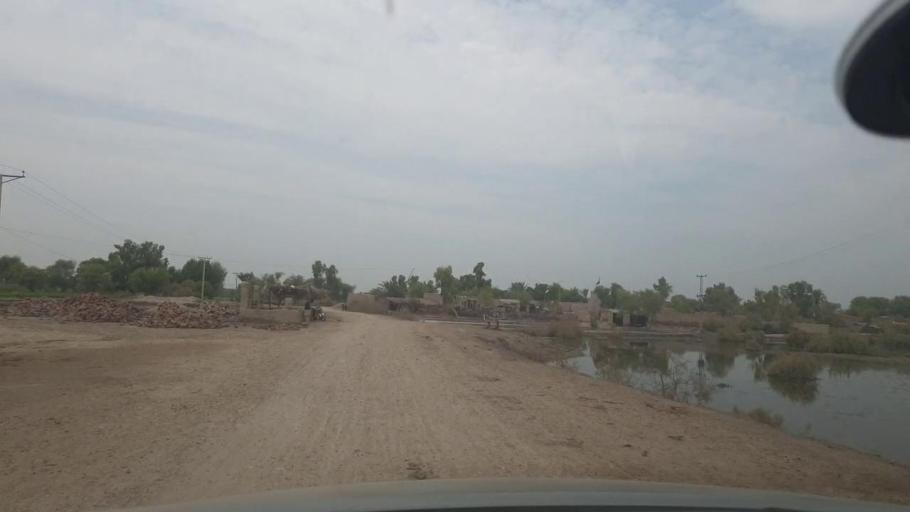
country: PK
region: Balochistan
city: Mehrabpur
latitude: 28.0625
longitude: 68.1393
